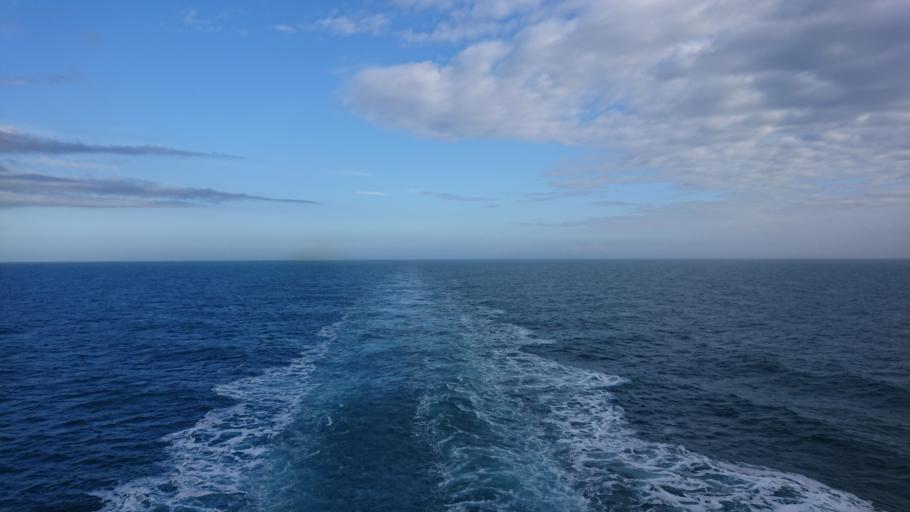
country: GB
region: Wales
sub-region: Pembrokeshire
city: Saint David's
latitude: 52.1359
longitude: -5.6235
